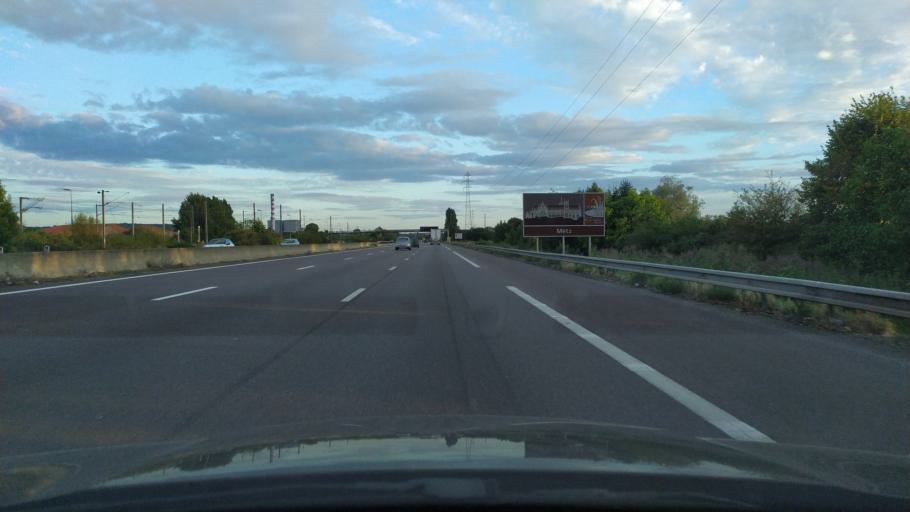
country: FR
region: Lorraine
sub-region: Departement de la Moselle
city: Argancy
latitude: 49.1741
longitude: 6.1791
